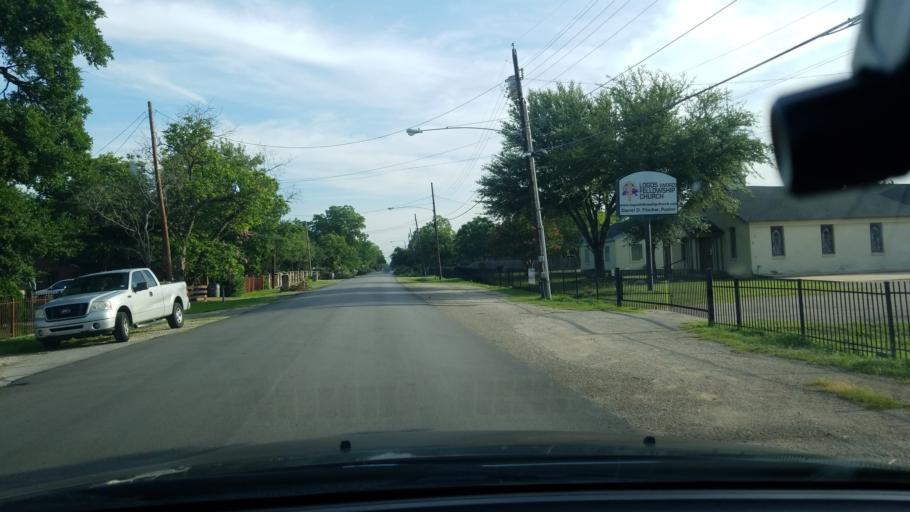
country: US
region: Texas
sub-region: Dallas County
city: Balch Springs
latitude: 32.7263
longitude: -96.6884
